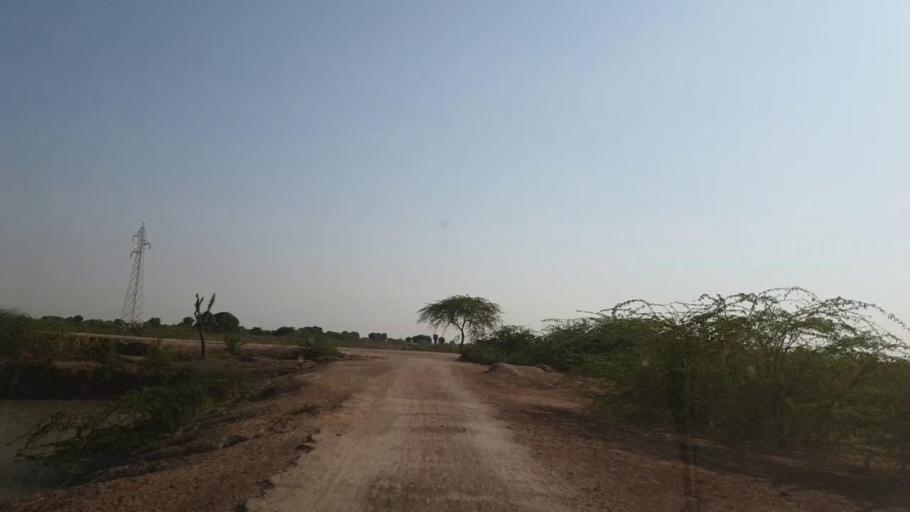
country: PK
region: Sindh
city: Naukot
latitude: 25.0188
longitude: 69.4696
